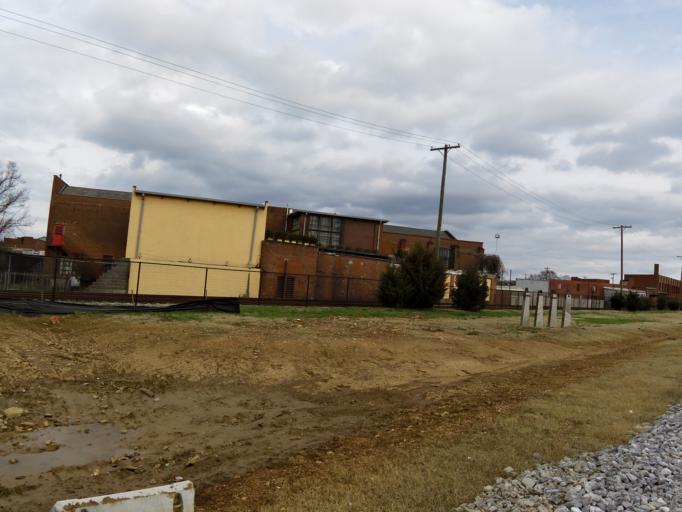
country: US
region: Tennessee
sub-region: Hamilton County
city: Chattanooga
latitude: 35.0282
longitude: -85.2929
